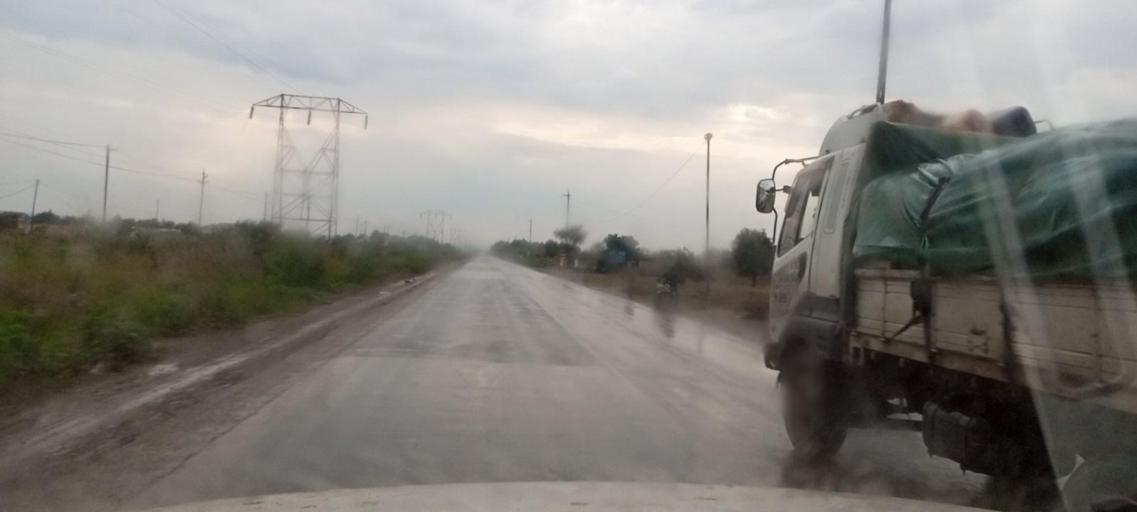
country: CD
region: Katanga
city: Likasi
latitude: -11.0034
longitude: 26.8188
